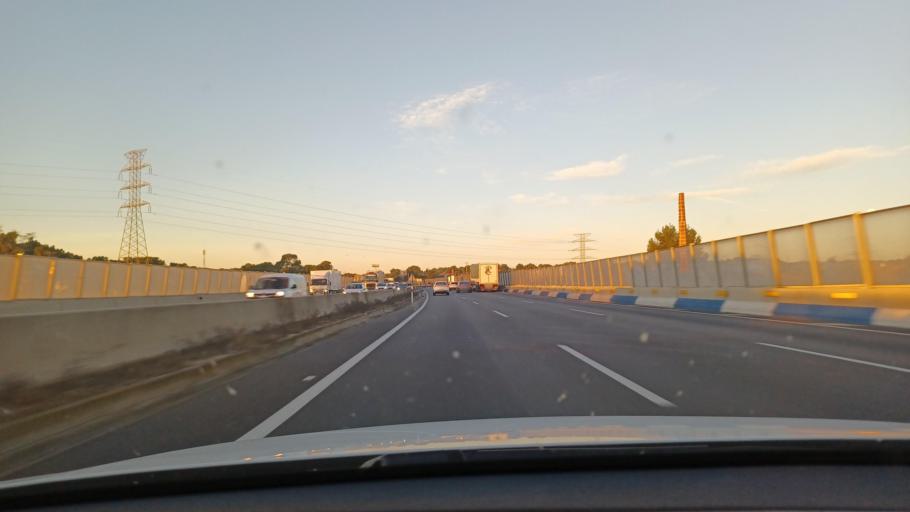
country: ES
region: Valencia
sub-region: Provincia de Valencia
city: Manises
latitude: 39.5124
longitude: -0.4982
